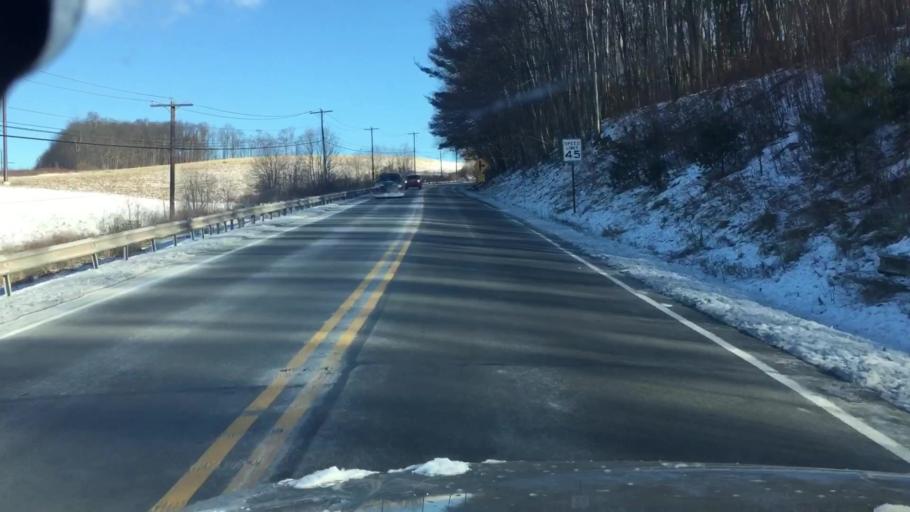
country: US
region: Pennsylvania
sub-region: Luzerne County
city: Nescopeck
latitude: 41.0534
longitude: -76.1728
